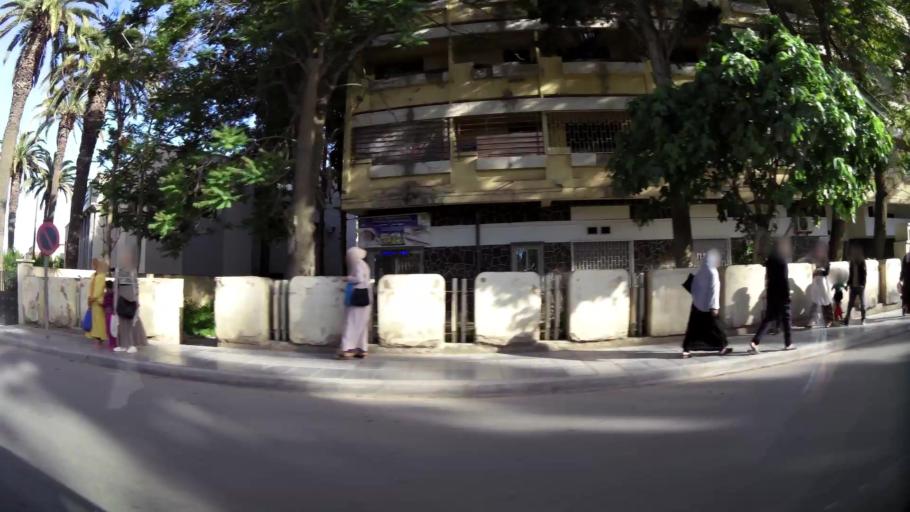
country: MA
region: Oriental
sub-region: Oujda-Angad
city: Oujda
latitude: 34.6769
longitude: -1.9129
